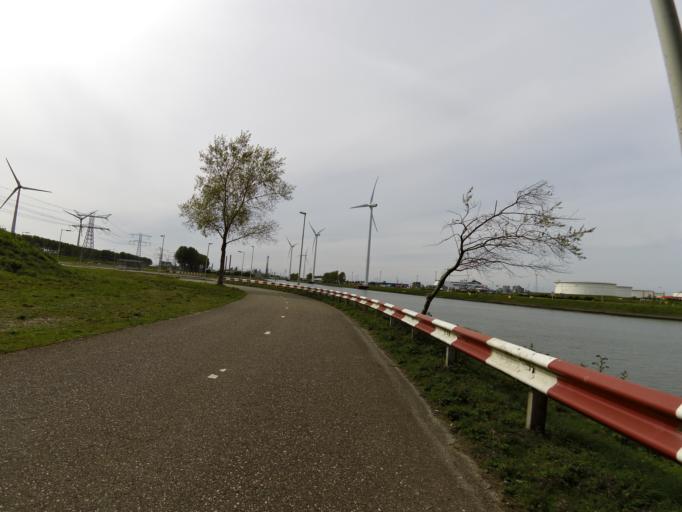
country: NL
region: South Holland
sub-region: Gemeente Brielle
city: Brielle
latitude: 51.9359
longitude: 4.1392
